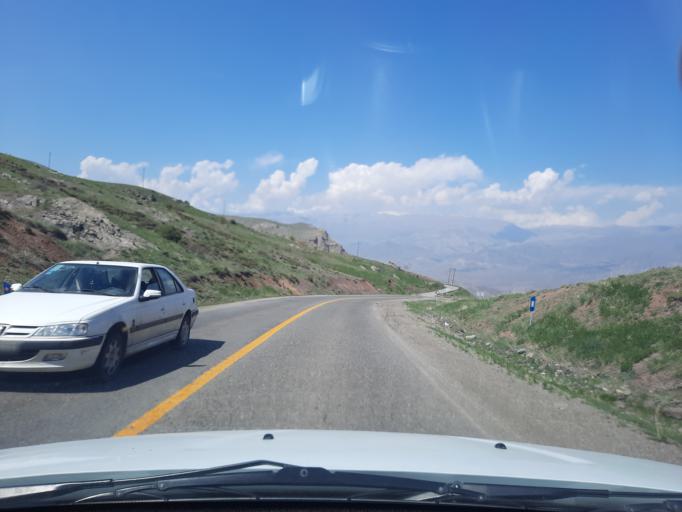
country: IR
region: Qazvin
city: Qazvin
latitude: 36.4056
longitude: 50.2253
